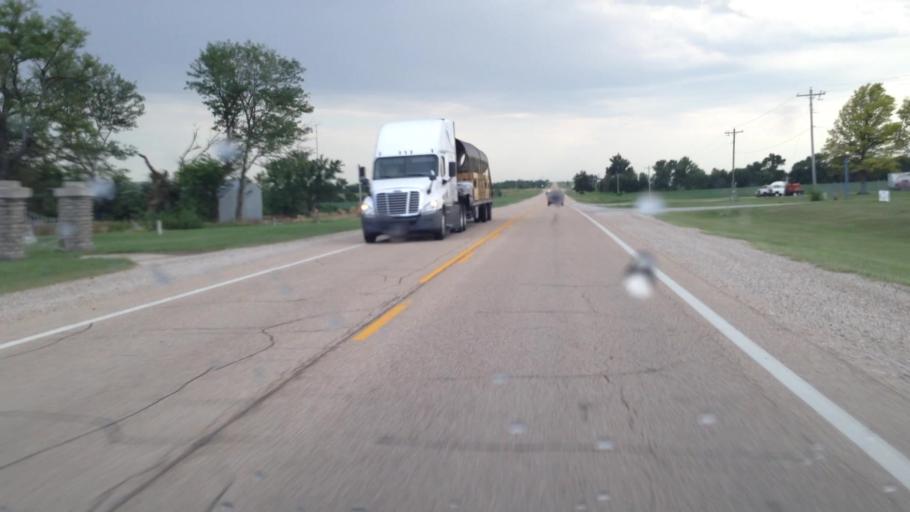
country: US
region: Kansas
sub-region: Coffey County
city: Burlington
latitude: 38.1782
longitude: -95.7388
